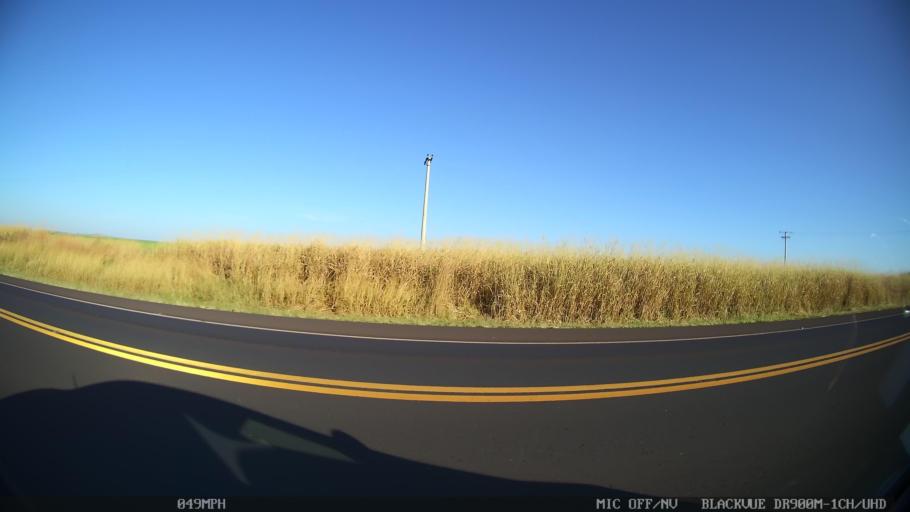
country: BR
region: Sao Paulo
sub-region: Guapiacu
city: Guapiacu
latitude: -20.7473
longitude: -49.1221
